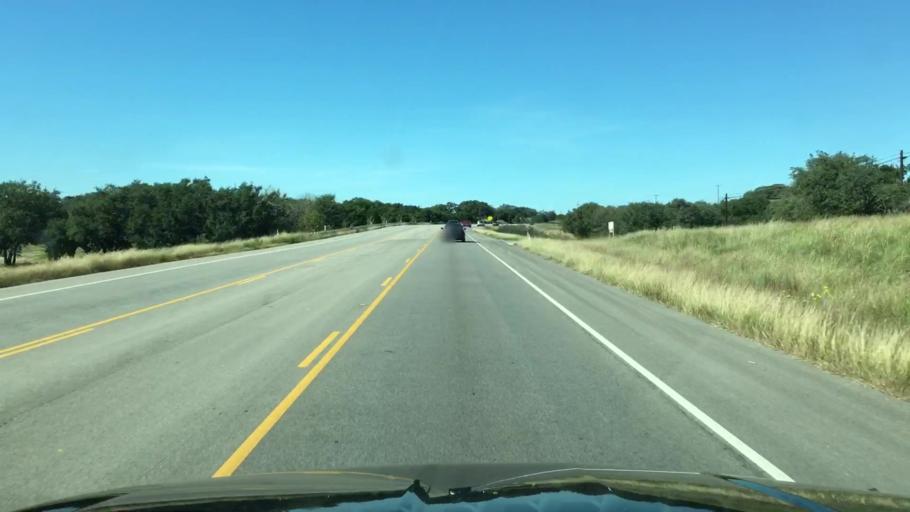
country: US
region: Texas
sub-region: Hays County
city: Dripping Springs
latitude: 30.1976
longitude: -98.1739
